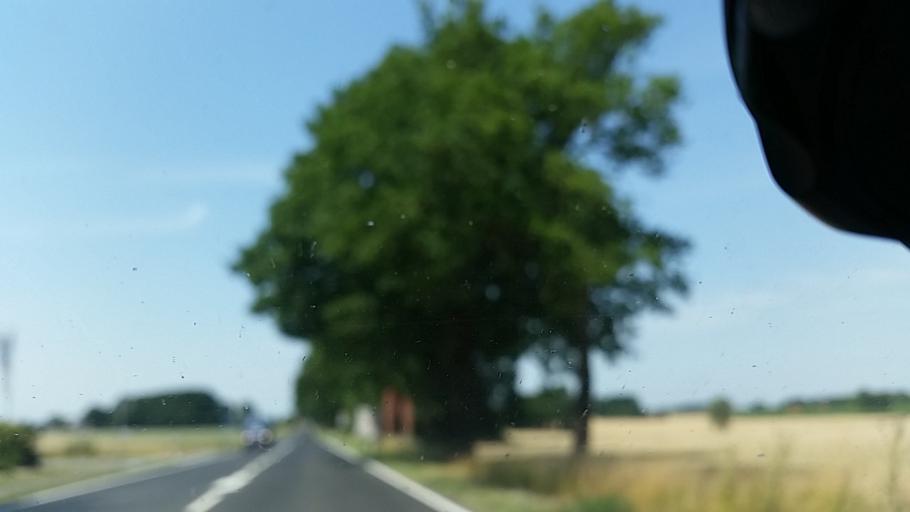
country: DE
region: Lower Saxony
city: Wietzen
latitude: 52.7286
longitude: 9.0418
